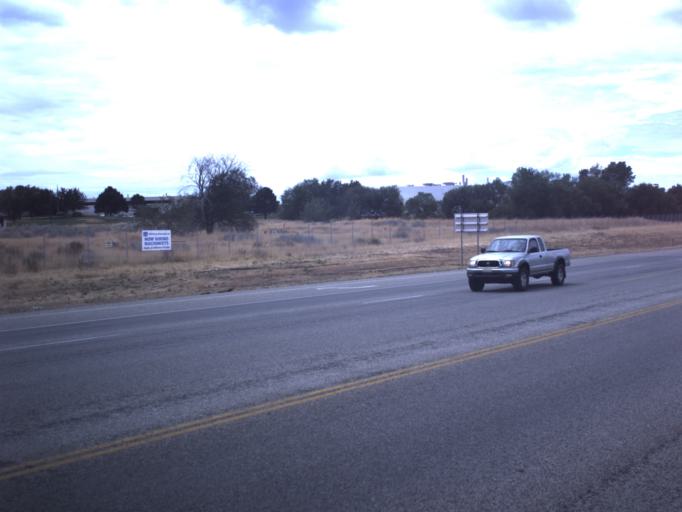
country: US
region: Utah
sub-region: Weber County
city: Riverdale
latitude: 41.2047
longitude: -112.0073
